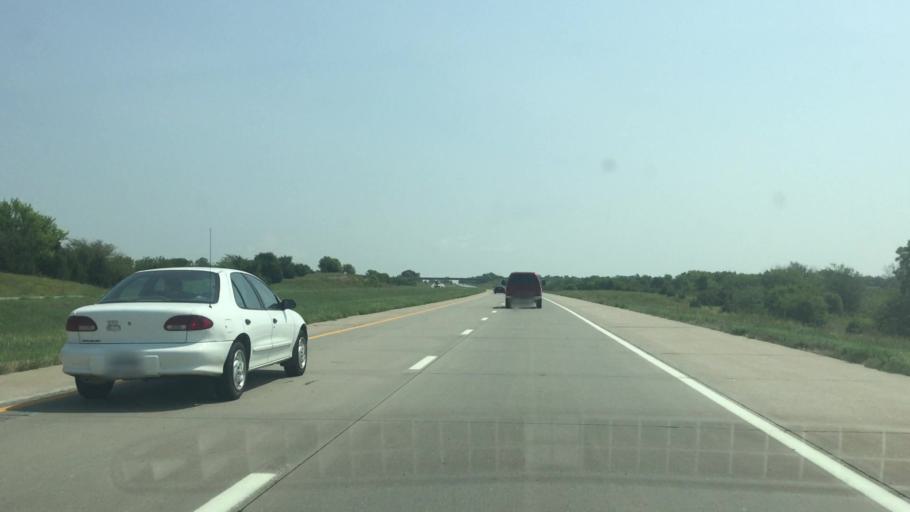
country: US
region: Kansas
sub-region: Osage County
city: Lyndon
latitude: 38.4534
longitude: -95.5745
